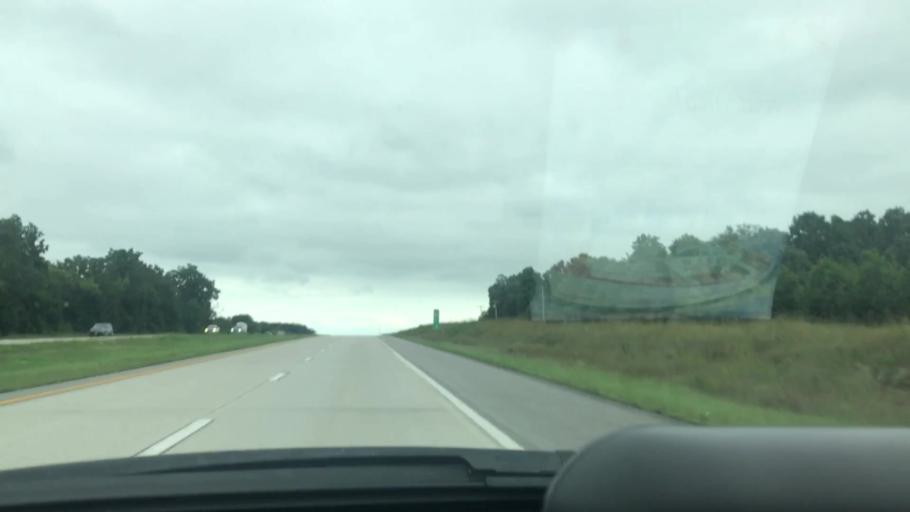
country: US
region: Missouri
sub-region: Greene County
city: Fair Grove
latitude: 37.4825
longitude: -93.1392
